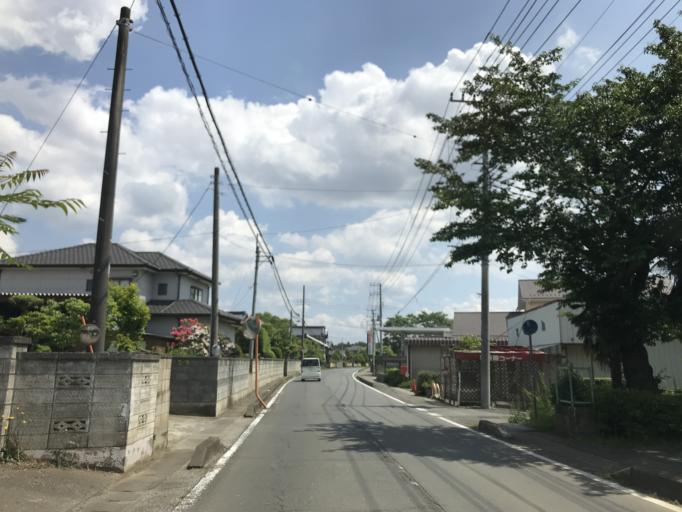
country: JP
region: Ibaraki
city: Mitsukaido
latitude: 36.0578
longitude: 140.0362
